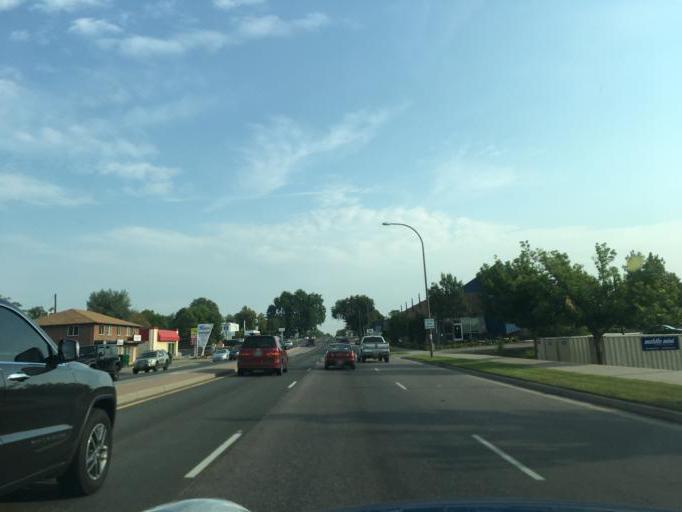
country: US
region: Colorado
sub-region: Jefferson County
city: Edgewater
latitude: 39.7425
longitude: -105.0814
